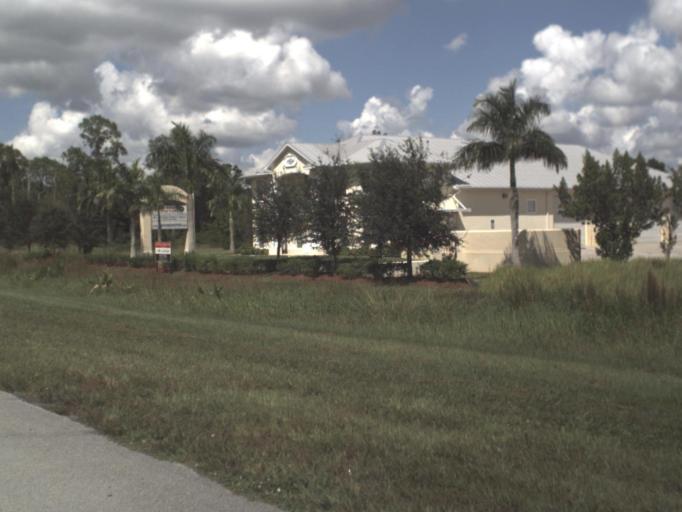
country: US
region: Florida
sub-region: Lee County
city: Gateway
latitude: 26.5949
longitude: -81.7405
